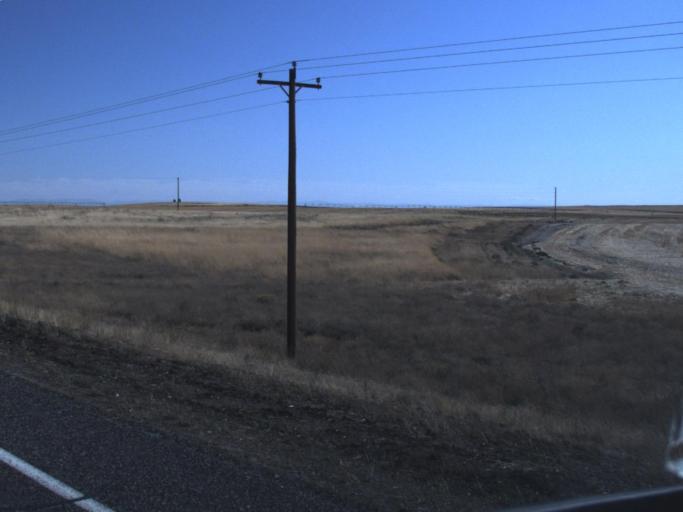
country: US
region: Washington
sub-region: Walla Walla County
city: Burbank
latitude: 46.2976
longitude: -118.7027
